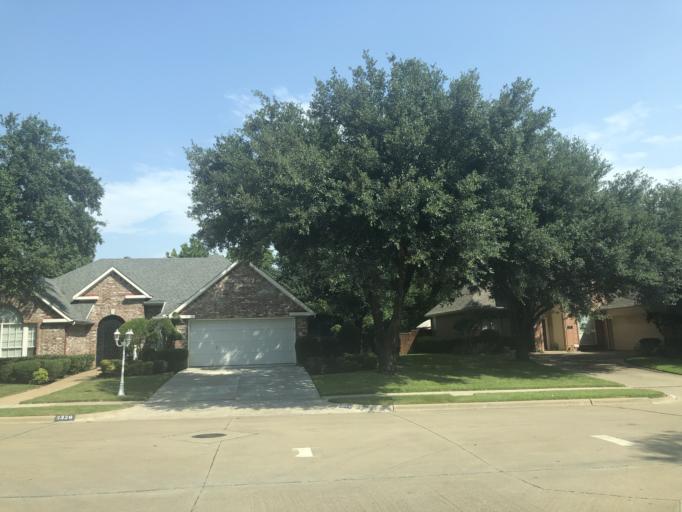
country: US
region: Texas
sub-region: Dallas County
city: Grand Prairie
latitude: 32.7664
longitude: -97.0370
